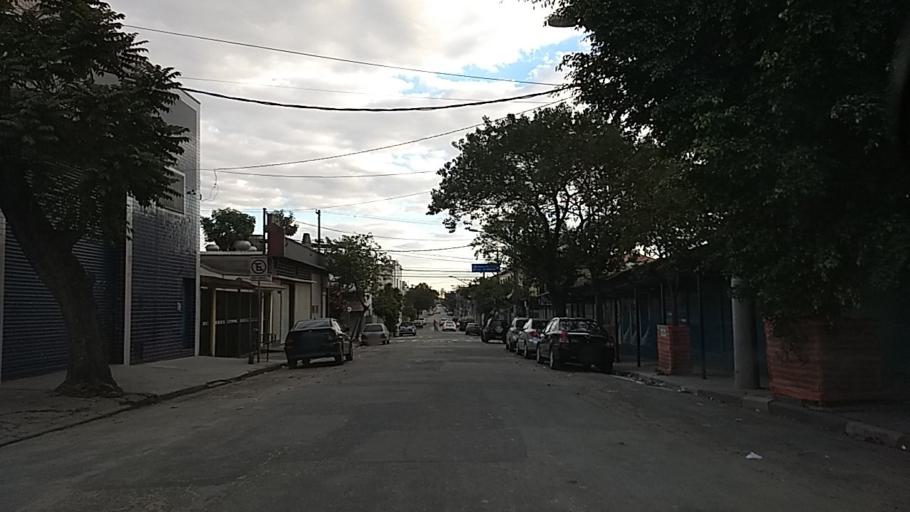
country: BR
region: Sao Paulo
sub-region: Sao Paulo
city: Sao Paulo
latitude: -23.5183
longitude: -46.5841
